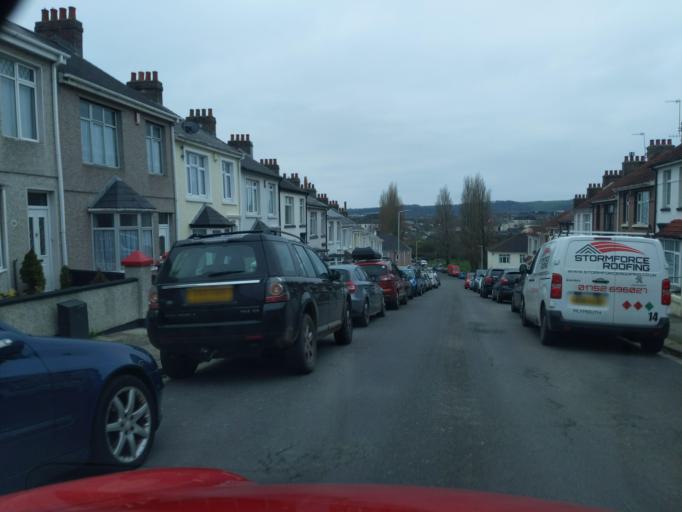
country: GB
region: England
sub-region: Plymouth
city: Plymouth
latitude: 50.3755
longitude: -4.1161
